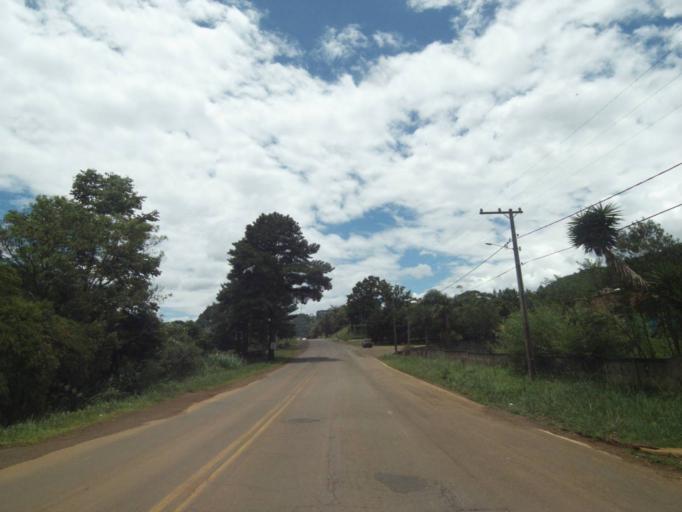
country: BR
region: Parana
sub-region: Pinhao
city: Pinhao
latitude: -26.1565
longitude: -51.5635
